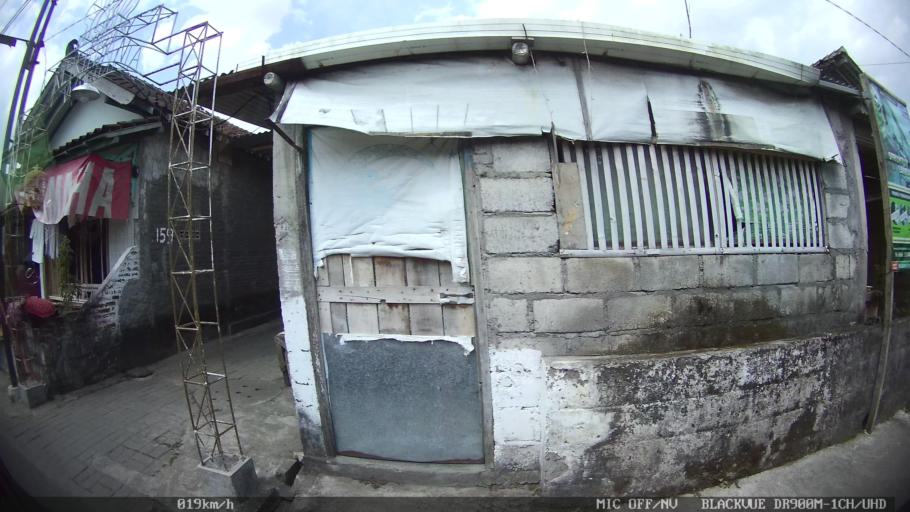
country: ID
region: Daerah Istimewa Yogyakarta
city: Gamping Lor
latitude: -7.8099
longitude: 110.3372
